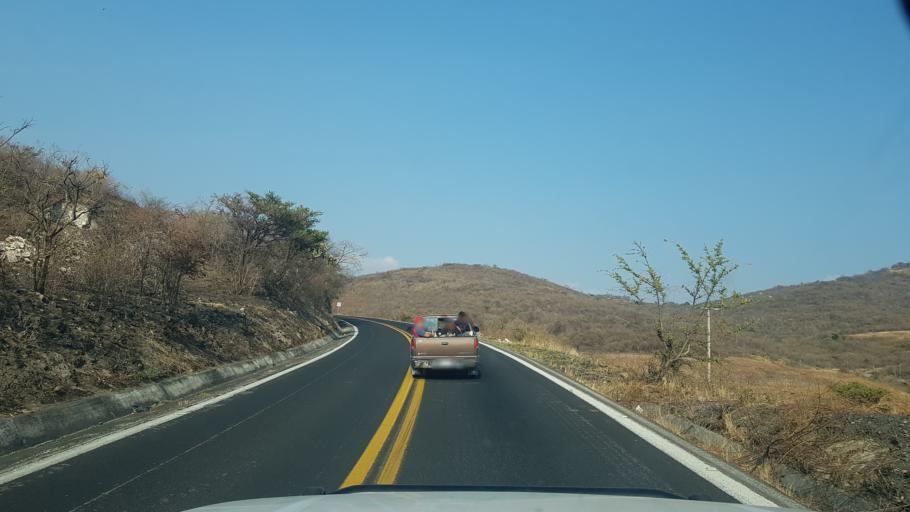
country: MX
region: Puebla
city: Calmeca
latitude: 18.6416
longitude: -98.6093
